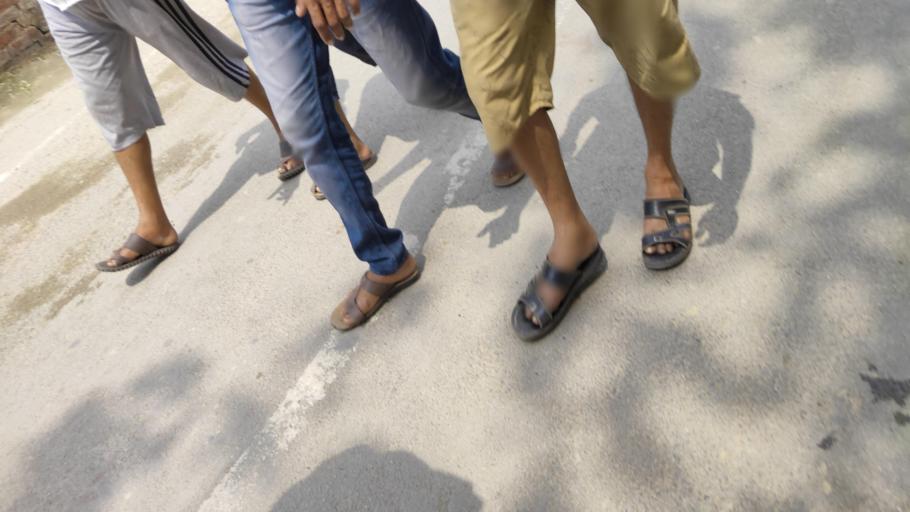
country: IN
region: Uttar Pradesh
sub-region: Faizabad
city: Ayodhya
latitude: 26.7836
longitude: 82.1778
